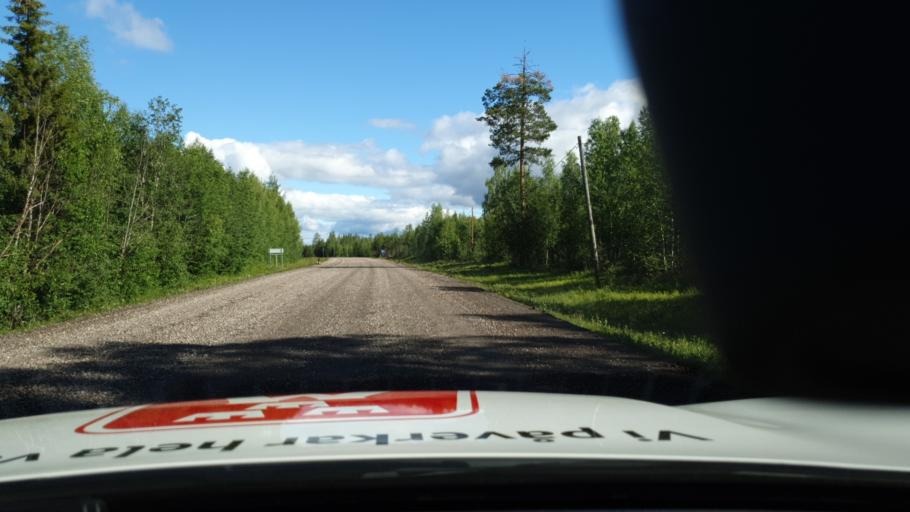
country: SE
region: Norrbotten
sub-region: Alvsbyns Kommun
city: AElvsbyn
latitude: 66.1937
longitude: 20.8854
